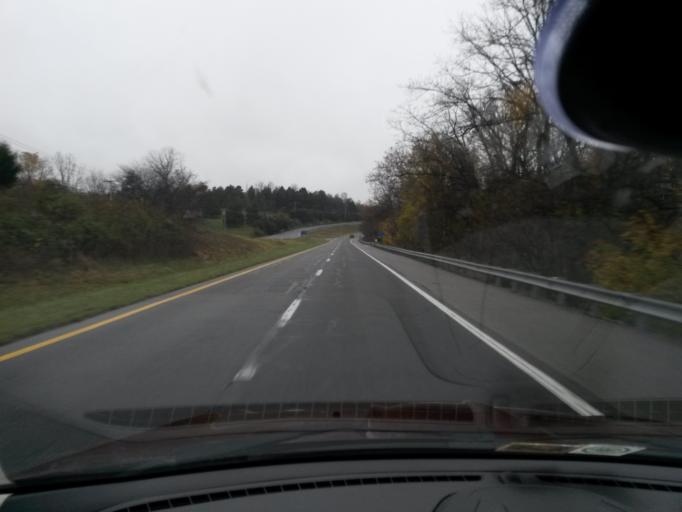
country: US
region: Virginia
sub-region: Botetourt County
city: Fincastle
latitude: 37.4683
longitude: -79.8818
